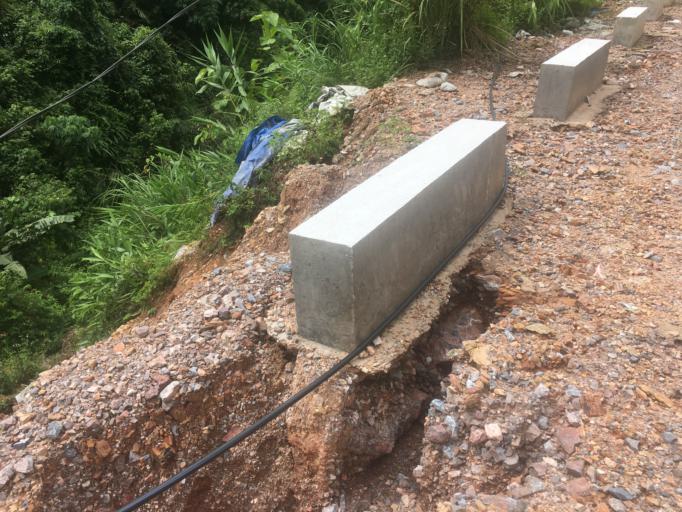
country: VN
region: Ha Giang
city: Thanh Pho Ha Giang
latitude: 22.8566
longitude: 105.0250
